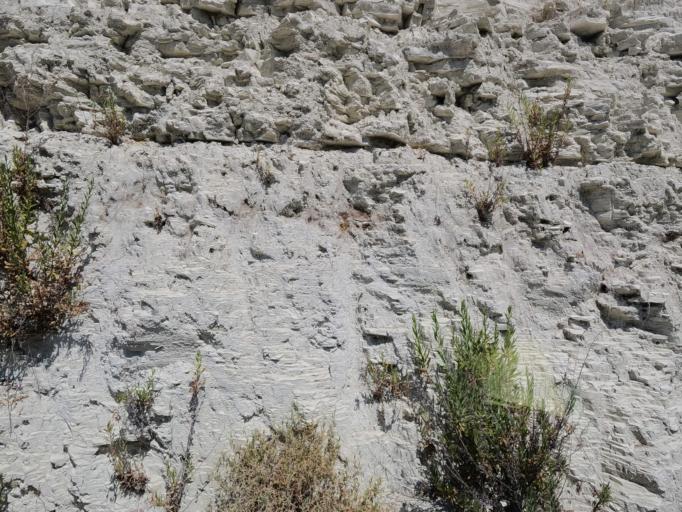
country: CY
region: Limassol
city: Pachna
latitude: 34.8175
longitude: 32.7496
